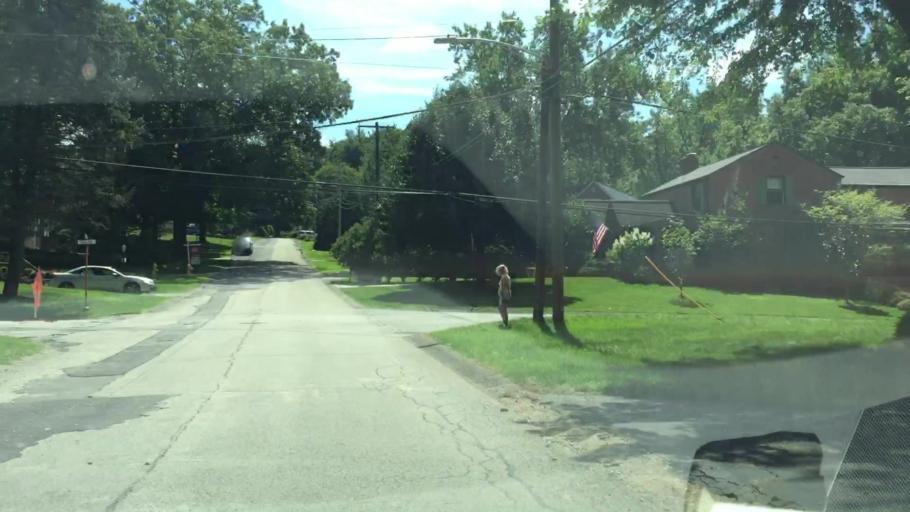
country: US
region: Pennsylvania
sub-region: Allegheny County
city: Bethel Park
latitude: 40.3175
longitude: -80.0521
